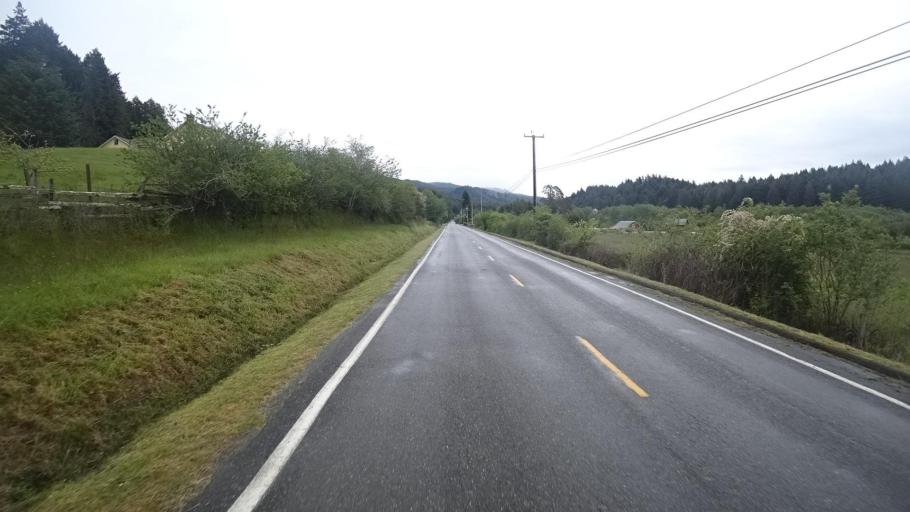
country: US
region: California
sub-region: Humboldt County
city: Bayside
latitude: 40.8369
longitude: -124.0519
